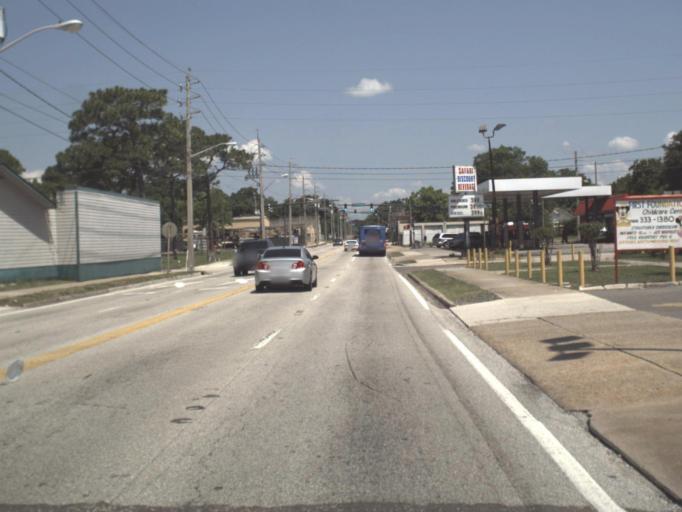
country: US
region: Florida
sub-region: Duval County
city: Jacksonville
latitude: 30.3747
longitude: -81.6662
